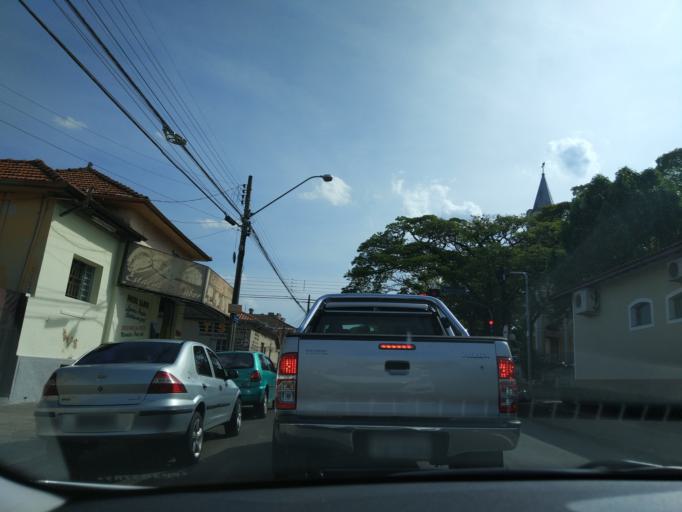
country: BR
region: Sao Paulo
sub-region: Botucatu
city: Botucatu
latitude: -22.8713
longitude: -48.4464
